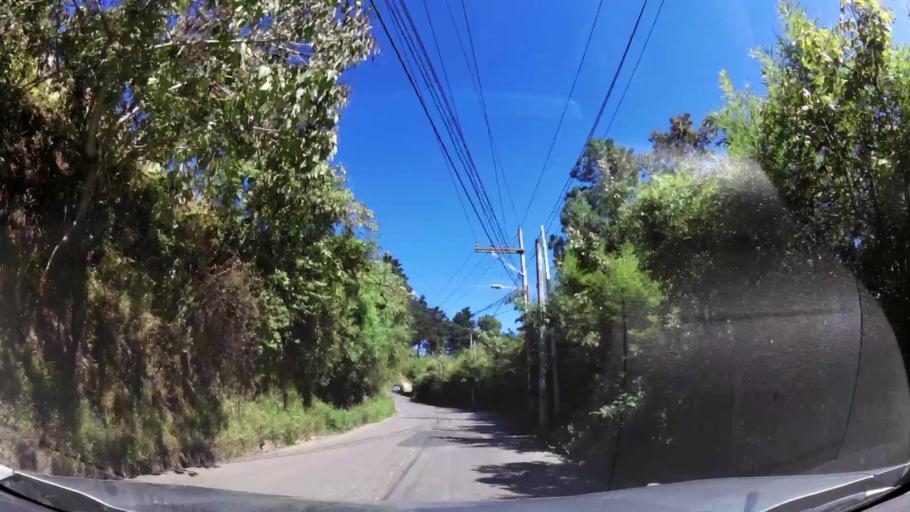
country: GT
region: Guatemala
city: San Jose Pinula
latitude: 14.5164
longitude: -90.4241
